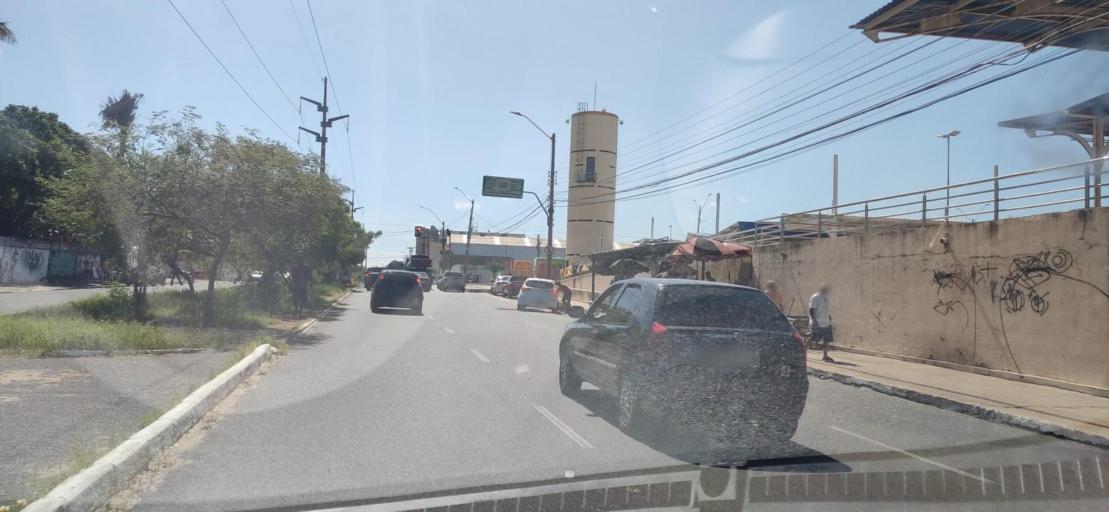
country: BR
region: Piaui
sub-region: Teresina
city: Teresina
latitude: -5.1200
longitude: -42.8038
